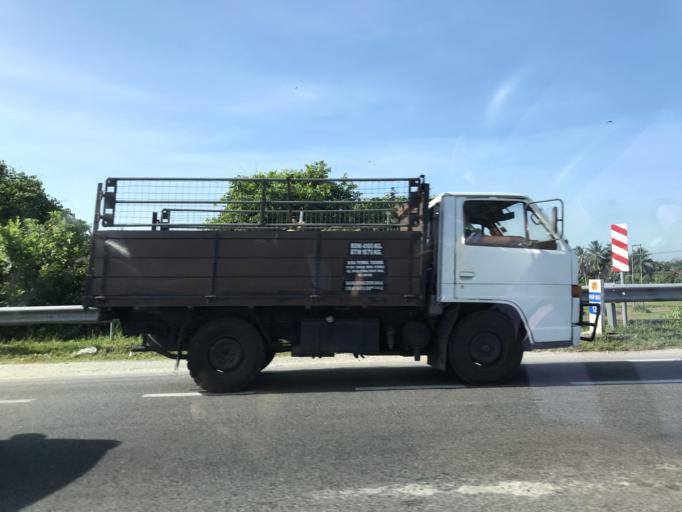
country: MY
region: Kelantan
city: Kampong Kadok
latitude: 6.0498
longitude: 102.2202
